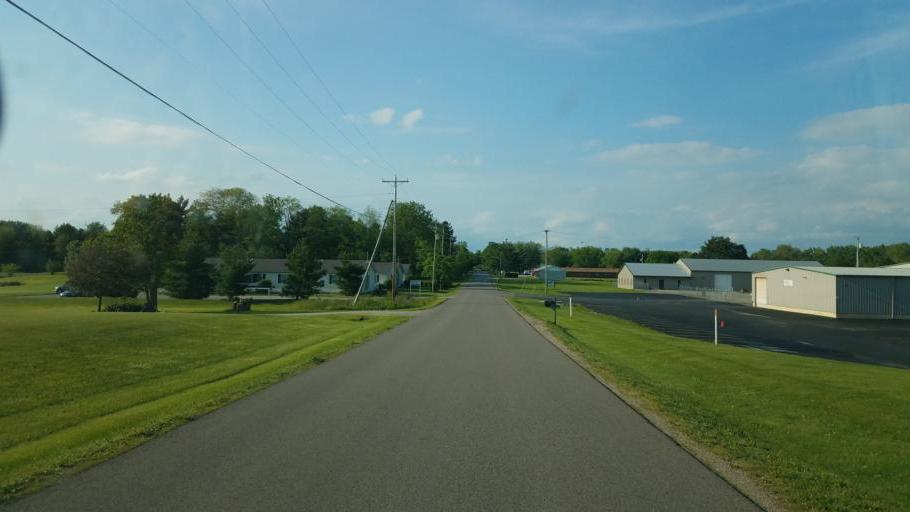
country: US
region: Ohio
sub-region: Morrow County
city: Cardington
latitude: 40.3912
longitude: -82.8126
